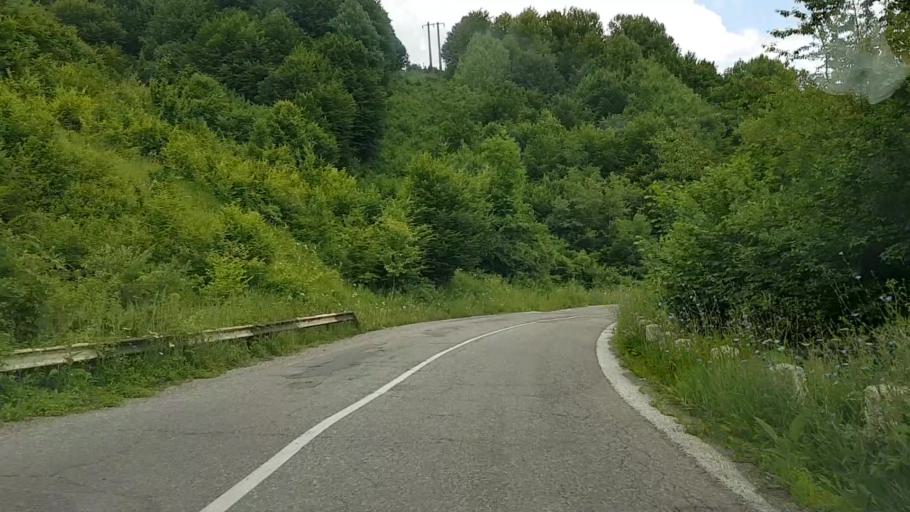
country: RO
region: Neamt
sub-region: Comuna Pangarati
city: Pangarati
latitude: 46.9577
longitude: 26.1248
